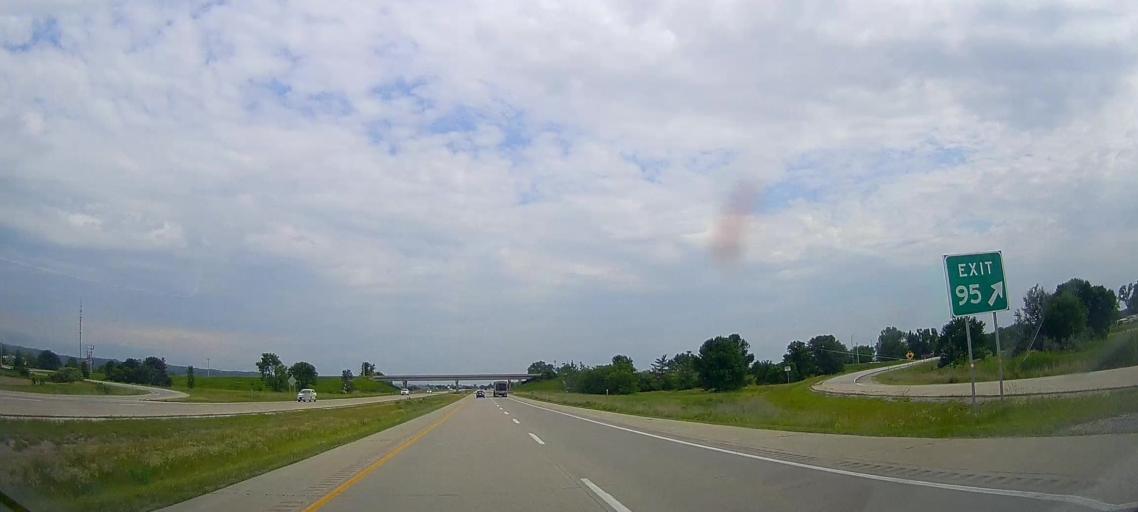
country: US
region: Nebraska
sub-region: Burt County
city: Tekamah
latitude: 41.8036
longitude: -96.0574
